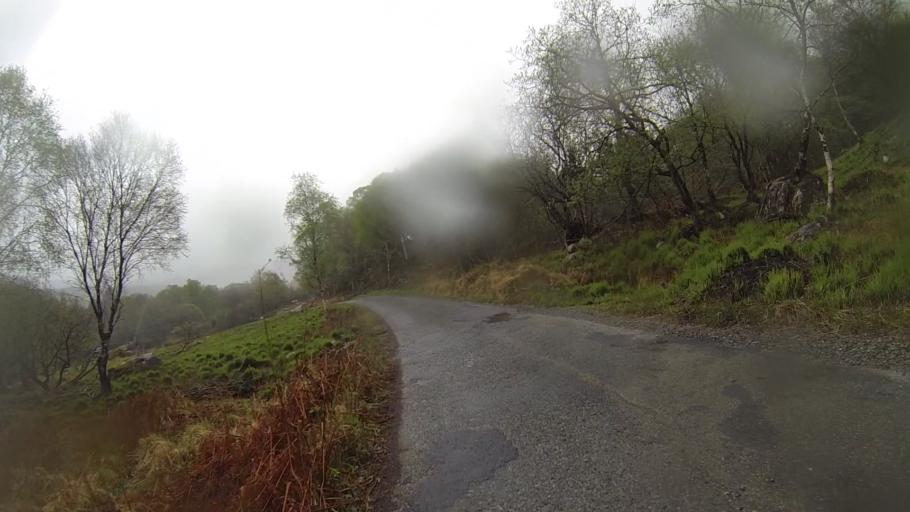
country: IE
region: Munster
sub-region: Ciarrai
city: Kenmare
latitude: 51.9634
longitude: -9.6362
